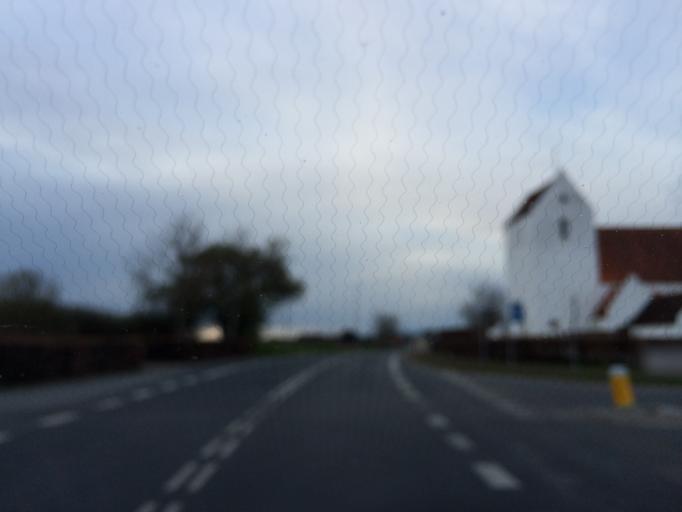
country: DK
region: South Denmark
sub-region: Odense Kommune
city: Bellinge
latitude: 55.3507
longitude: 10.2766
